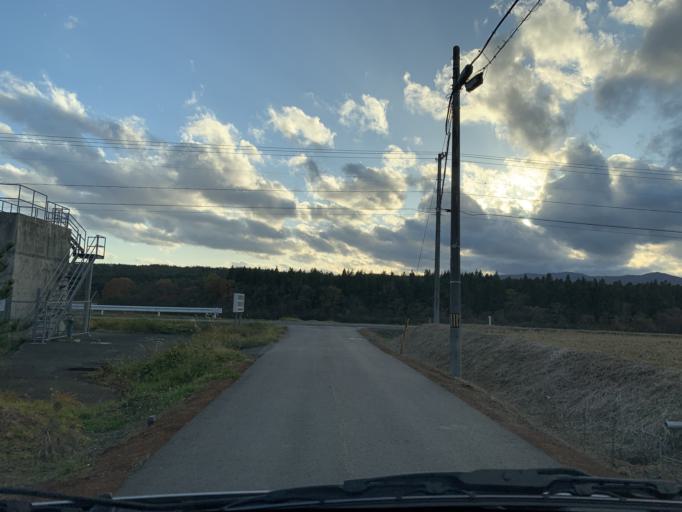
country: JP
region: Iwate
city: Mizusawa
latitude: 39.0828
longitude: 141.0326
